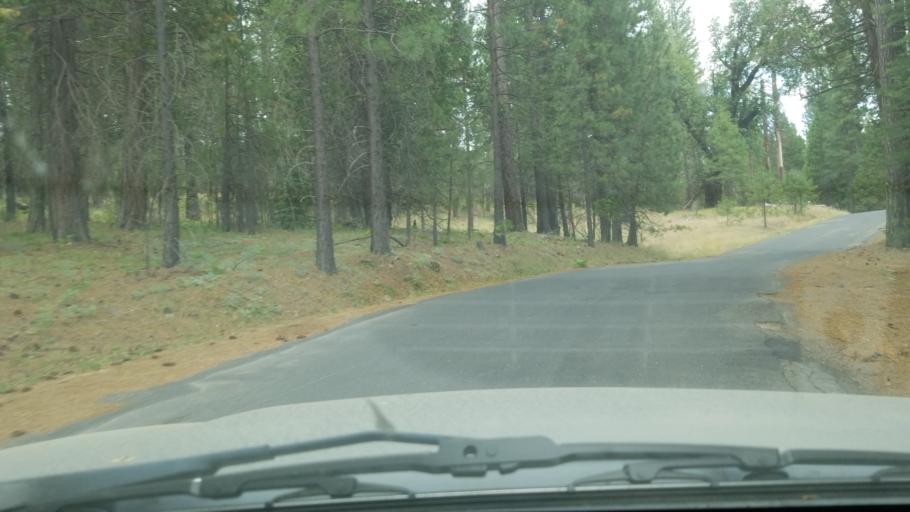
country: US
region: California
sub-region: Mariposa County
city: Yosemite Valley
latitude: 37.8491
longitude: -119.8584
